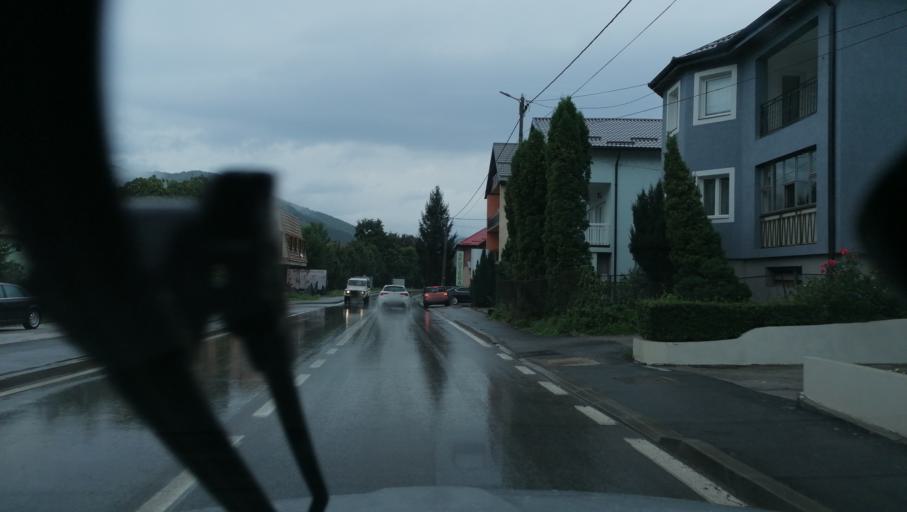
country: BA
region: Federation of Bosnia and Herzegovina
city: Gorazde
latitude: 43.6719
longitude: 18.9818
